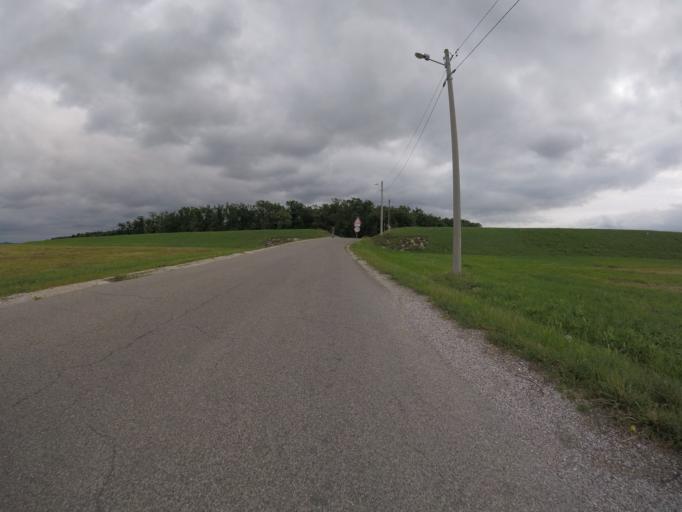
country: HR
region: Zagrebacka
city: Gradici
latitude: 45.6978
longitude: 16.0371
